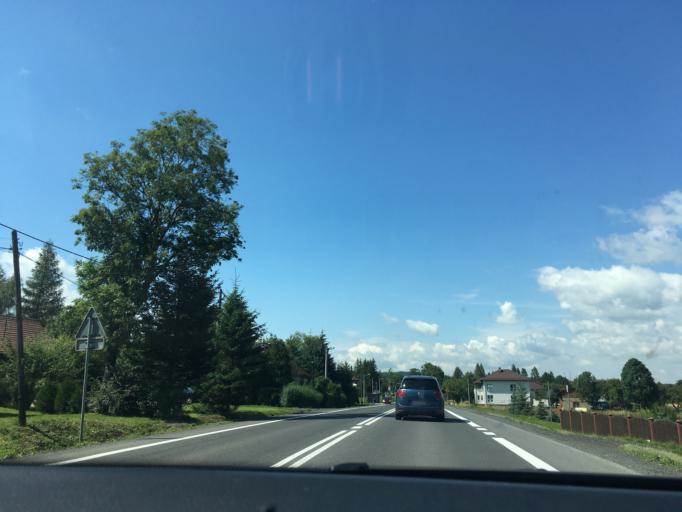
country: PL
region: Subcarpathian Voivodeship
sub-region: Powiat krosnienski
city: Dukla
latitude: 49.5390
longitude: 21.6935
